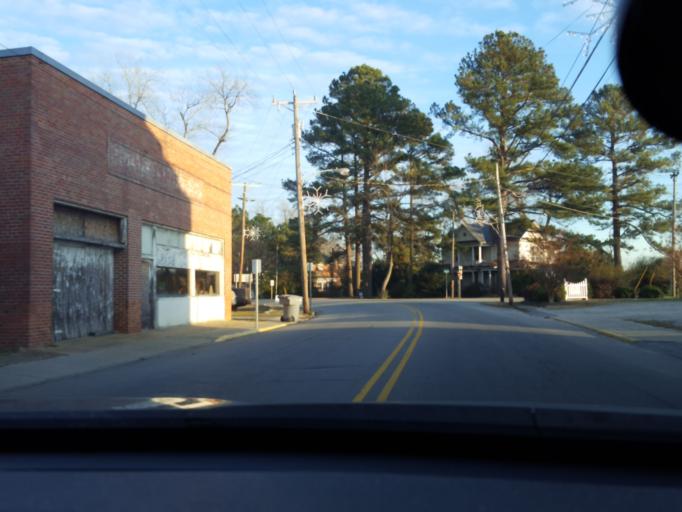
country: US
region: North Carolina
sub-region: Northampton County
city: Jackson
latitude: 36.2735
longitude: -77.2843
